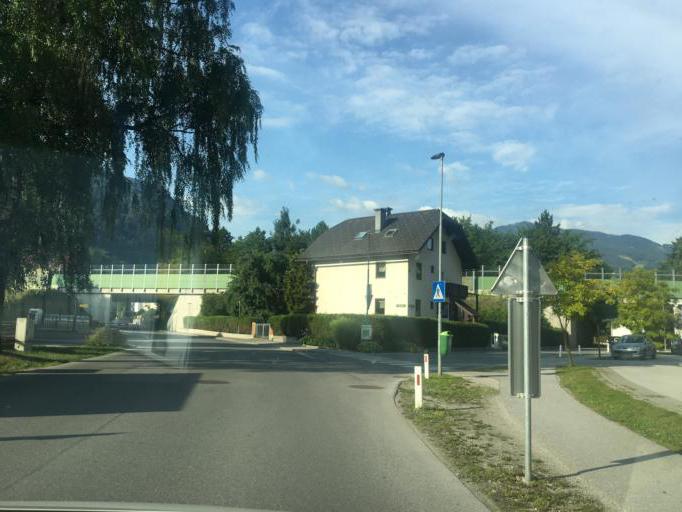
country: AT
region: Styria
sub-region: Politischer Bezirk Liezen
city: Schladming
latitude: 47.3972
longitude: 13.6925
